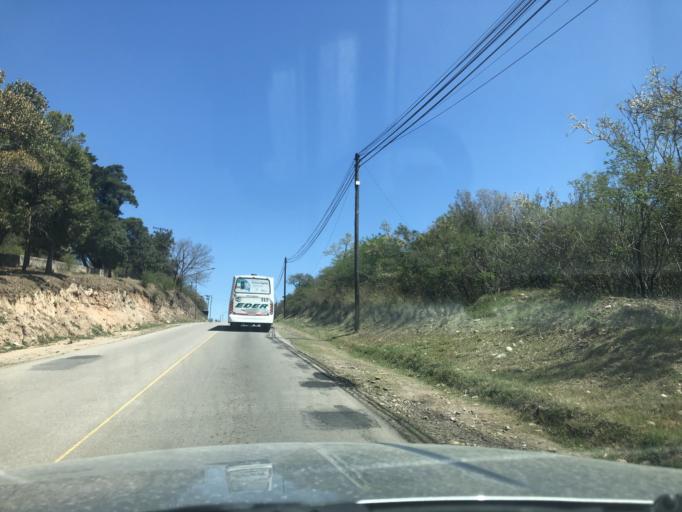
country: AR
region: Cordoba
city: La Granja
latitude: -31.0161
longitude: -64.2721
